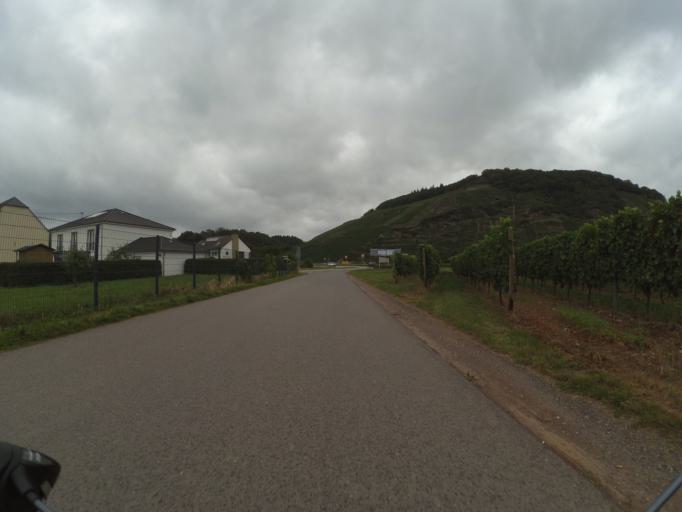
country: DE
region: Rheinland-Pfalz
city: Thornich
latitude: 49.8352
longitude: 6.8412
